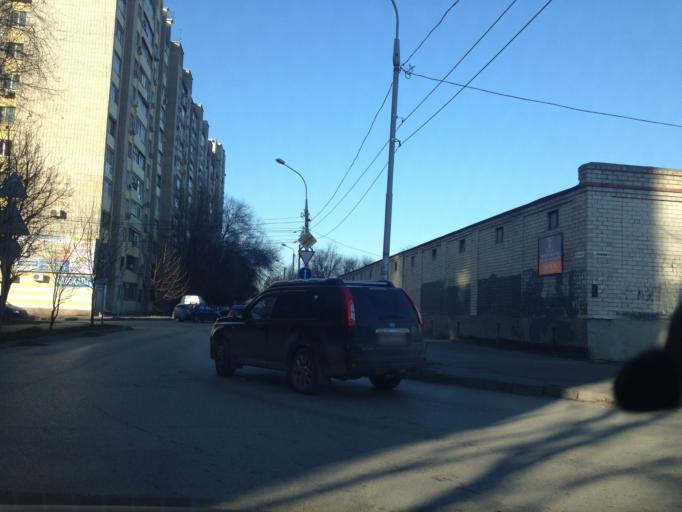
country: RU
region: Rostov
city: Rostov-na-Donu
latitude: 47.2338
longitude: 39.7188
